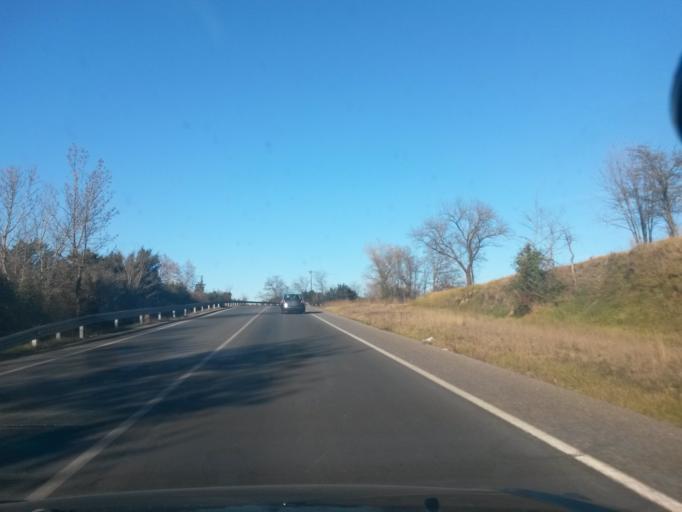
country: ES
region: Catalonia
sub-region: Provincia de Girona
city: Sarria de Ter
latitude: 42.0184
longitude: 2.8289
